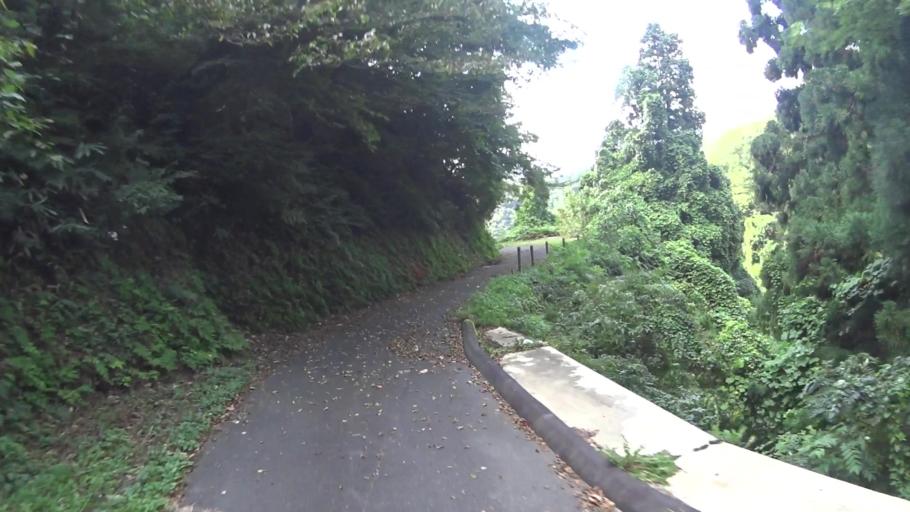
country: JP
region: Kyoto
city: Miyazu
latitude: 35.6635
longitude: 135.1345
